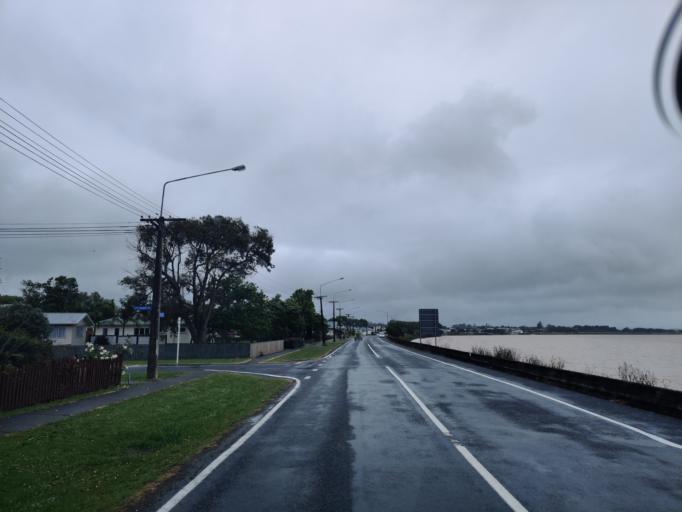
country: NZ
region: Northland
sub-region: Kaipara District
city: Dargaville
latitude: -35.9498
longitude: 173.8651
